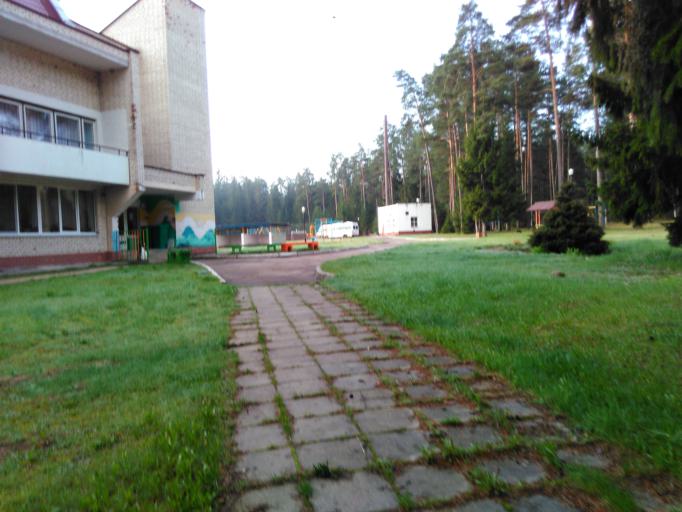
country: BY
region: Minsk
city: Rakaw
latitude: 53.9701
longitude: 27.0143
